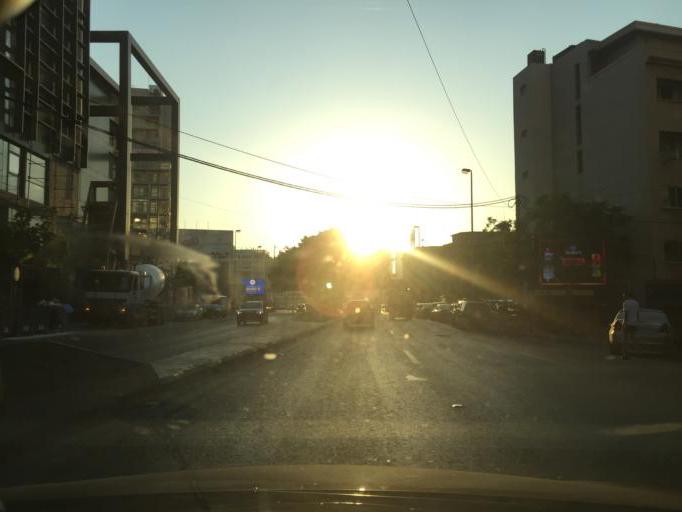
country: LB
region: Beyrouth
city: Beirut
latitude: 33.8973
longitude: 35.5114
